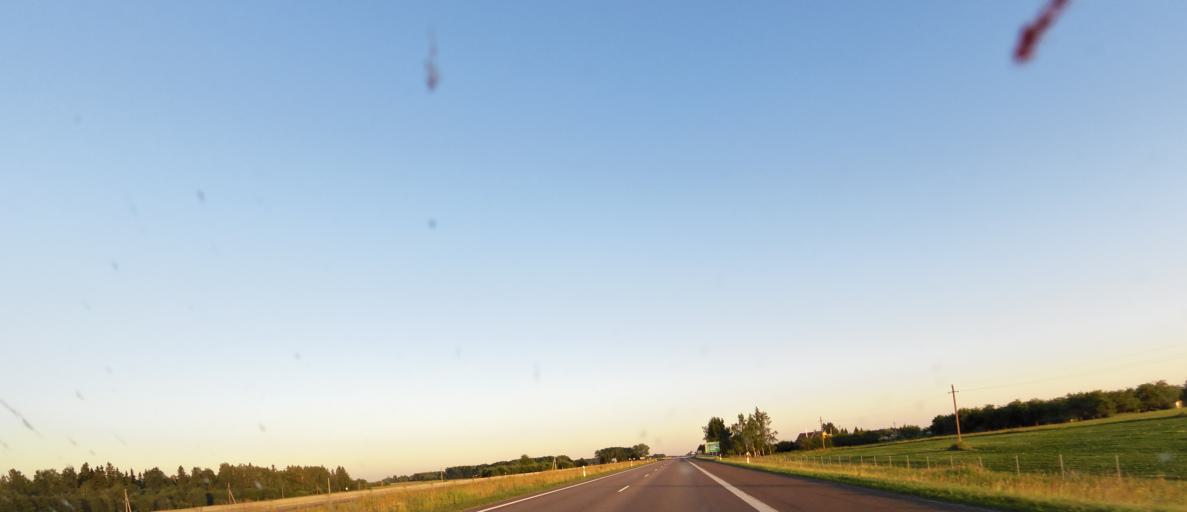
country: LT
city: Sirvintos
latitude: 55.0716
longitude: 24.8822
